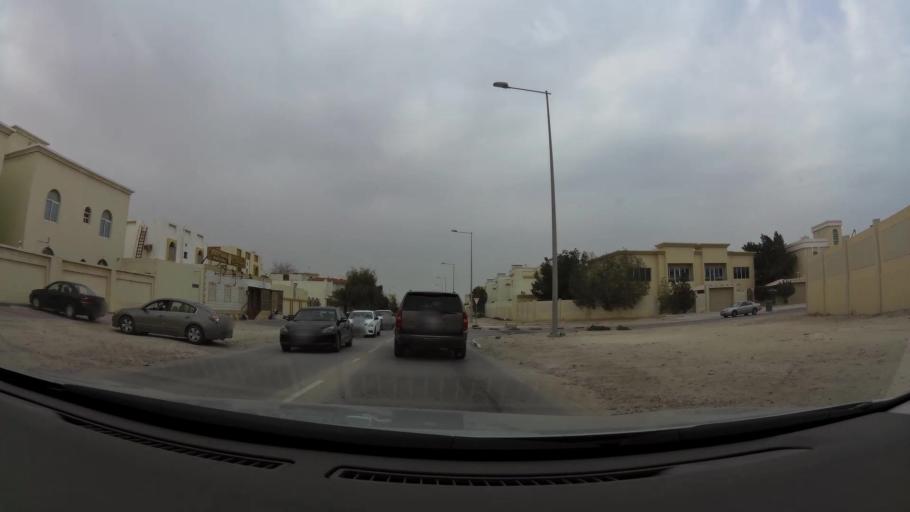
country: QA
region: Baladiyat ar Rayyan
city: Ar Rayyan
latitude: 25.3394
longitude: 51.4725
